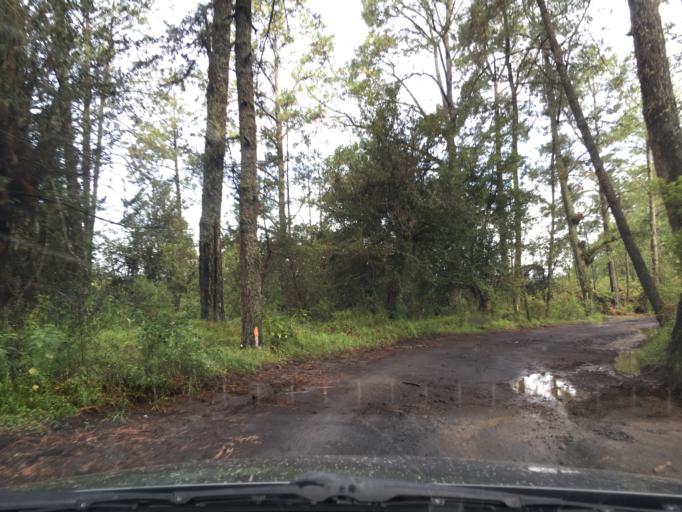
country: MX
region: Michoacan
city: Angahuan
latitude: 19.5165
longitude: -102.2201
